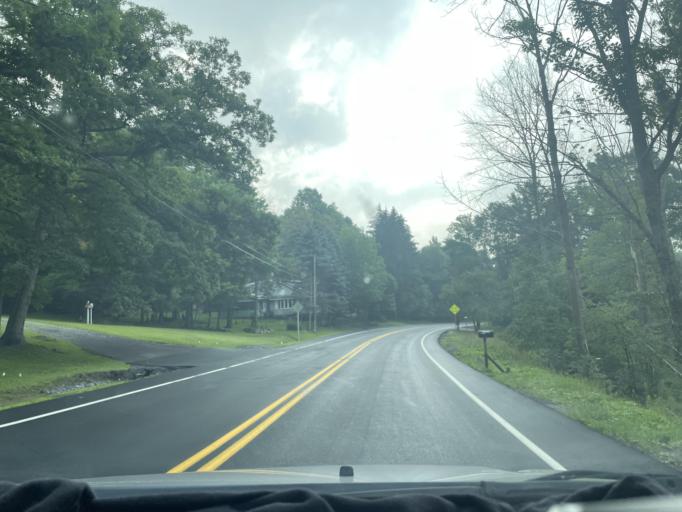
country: US
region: Maryland
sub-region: Garrett County
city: Mountain Lake Park
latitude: 39.3057
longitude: -79.4055
